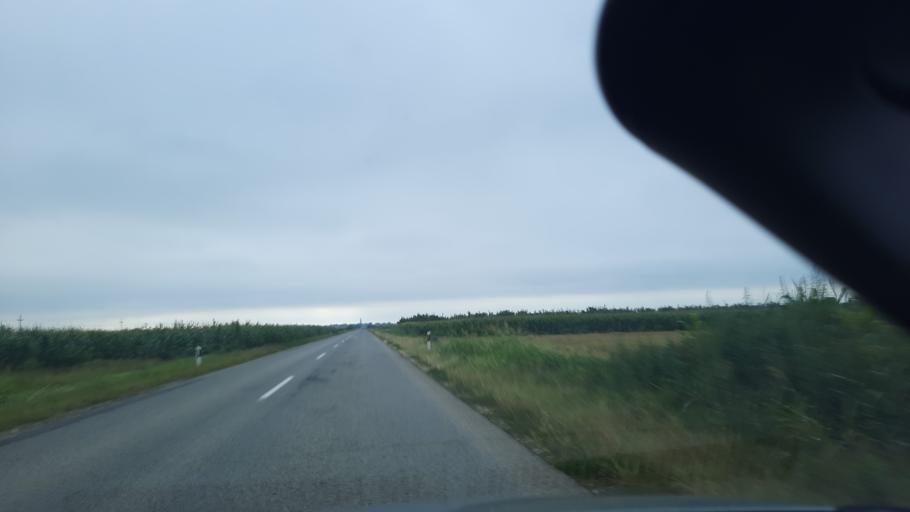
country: RS
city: Farkazdin
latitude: 45.1976
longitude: 20.4463
